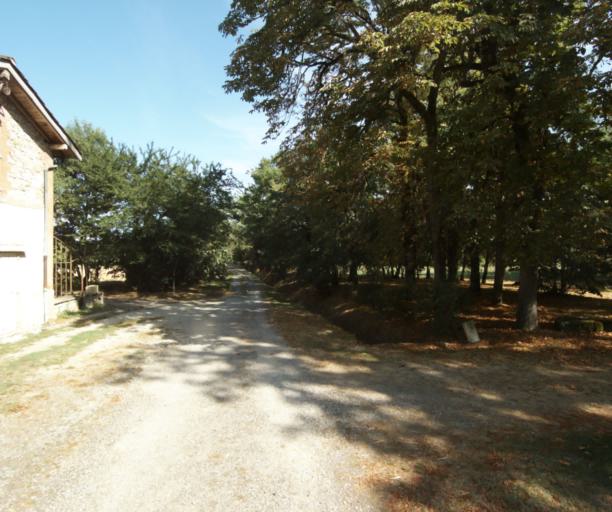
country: FR
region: Midi-Pyrenees
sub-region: Departement de la Haute-Garonne
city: Revel
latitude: 43.5075
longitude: 1.9808
